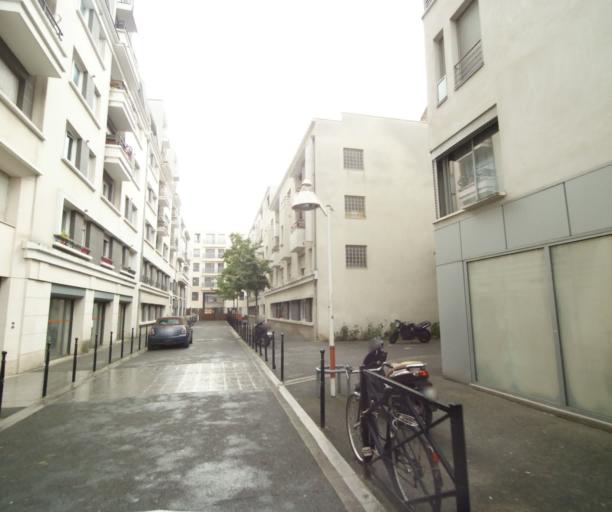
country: FR
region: Ile-de-France
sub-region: Departement des Hauts-de-Seine
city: Clichy
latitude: 48.9014
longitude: 2.3030
